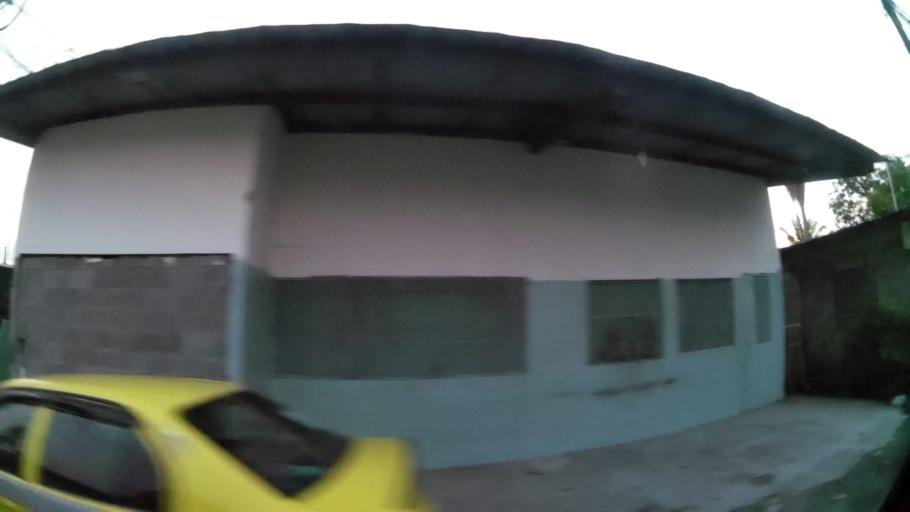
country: PA
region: Panama
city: Tocumen
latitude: 9.0809
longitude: -79.3959
